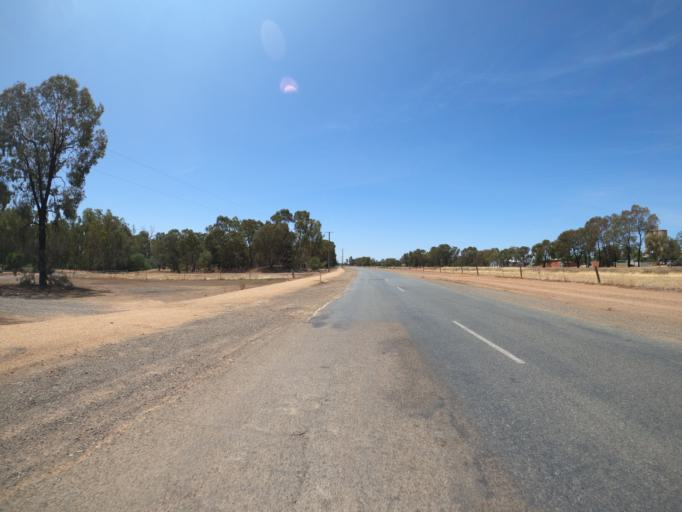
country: AU
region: Victoria
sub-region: Moira
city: Yarrawonga
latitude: -36.0163
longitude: 145.9958
